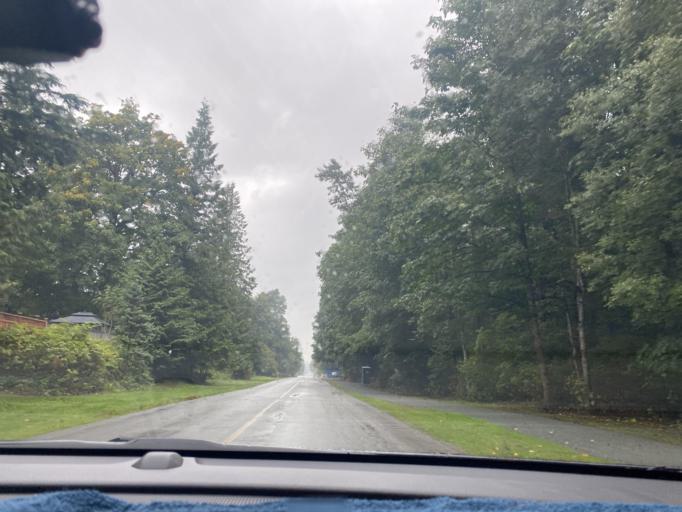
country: CA
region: British Columbia
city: Agassiz
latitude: 49.2831
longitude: -121.7775
